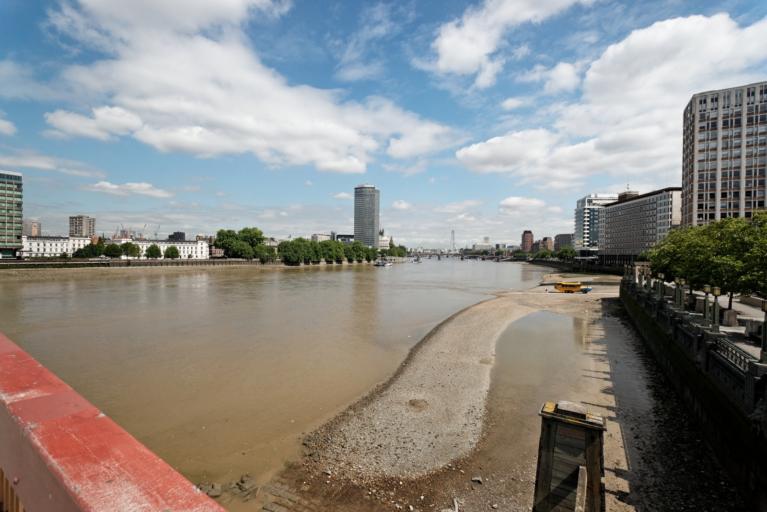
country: GB
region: England
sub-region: Greater London
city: City of Westminster
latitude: 51.4872
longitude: -0.1259
